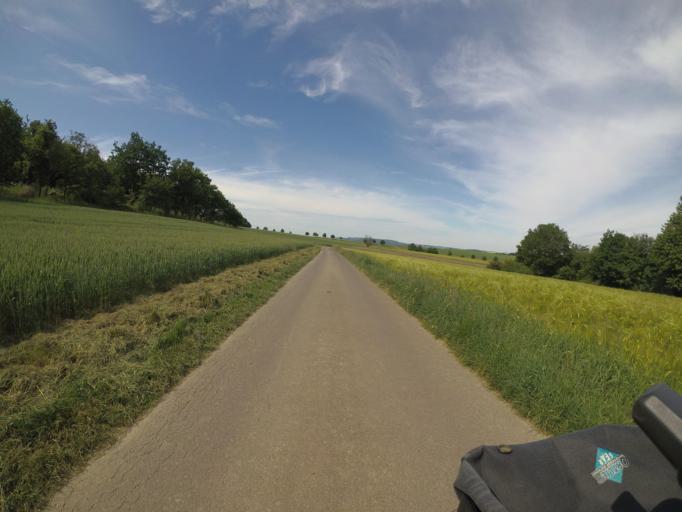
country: DE
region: Rheinland-Pfalz
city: Morbach
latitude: 49.8118
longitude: 7.0870
